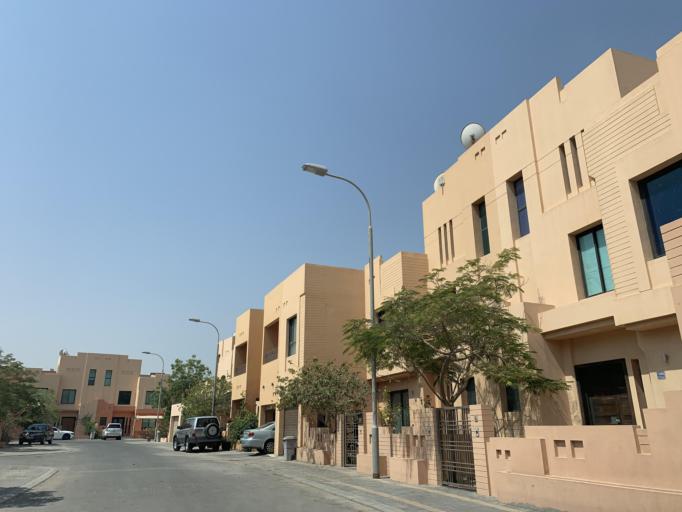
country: BH
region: Manama
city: Jidd Hafs
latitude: 26.2097
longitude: 50.5214
